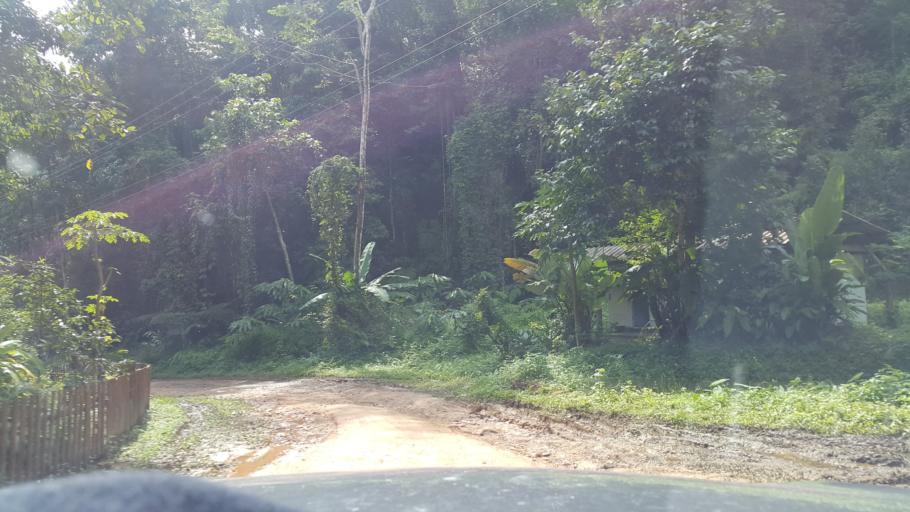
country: TH
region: Chiang Mai
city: Phrao
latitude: 19.1079
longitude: 99.2817
